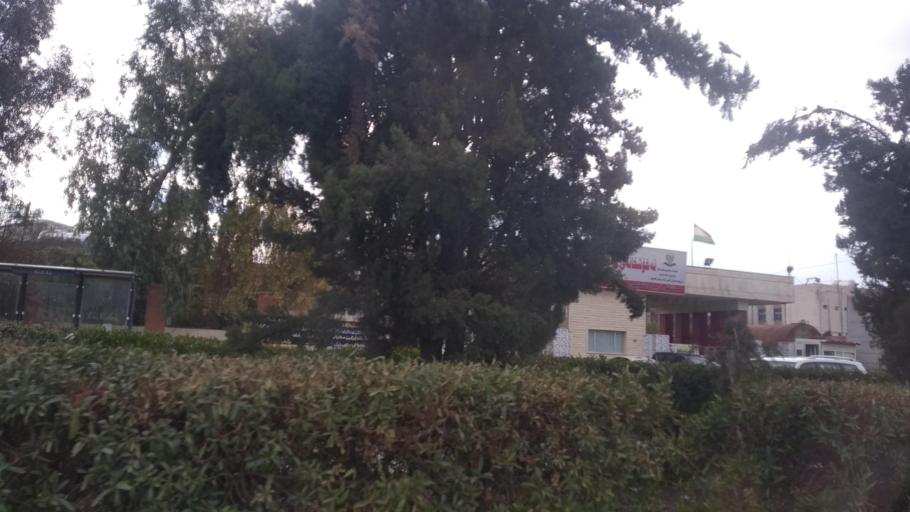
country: IQ
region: Arbil
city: Erbil
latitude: 36.1996
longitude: 44.0190
